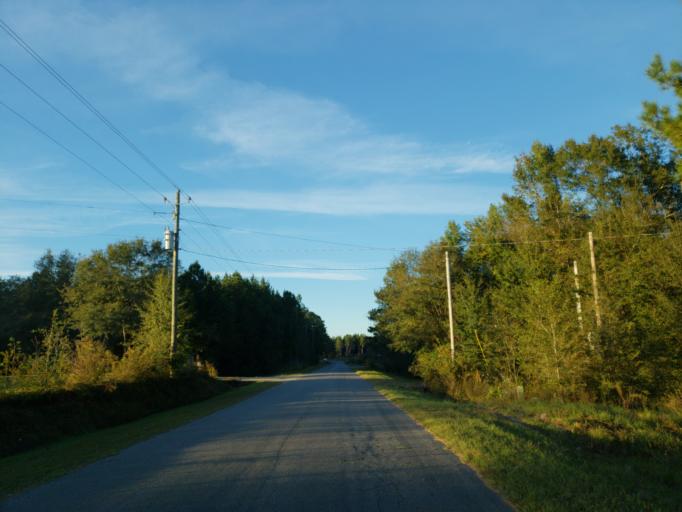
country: US
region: Mississippi
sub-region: Wayne County
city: Belmont
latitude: 31.4638
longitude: -88.5208
